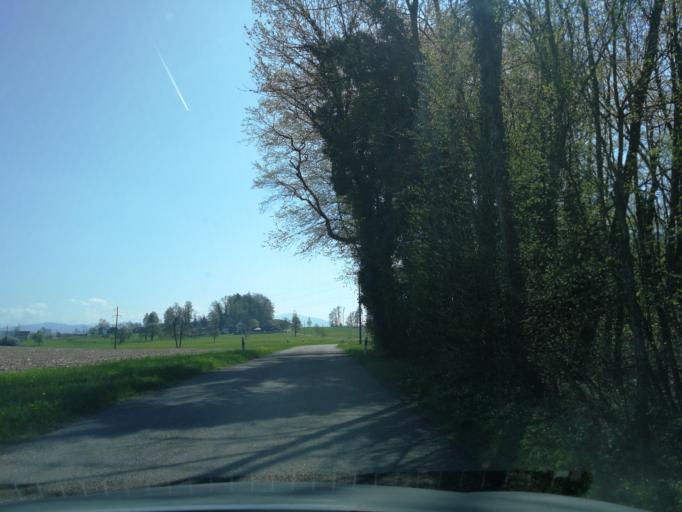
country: CH
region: Zurich
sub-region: Bezirk Hinwil
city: Wolfhausen
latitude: 47.2524
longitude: 8.8078
